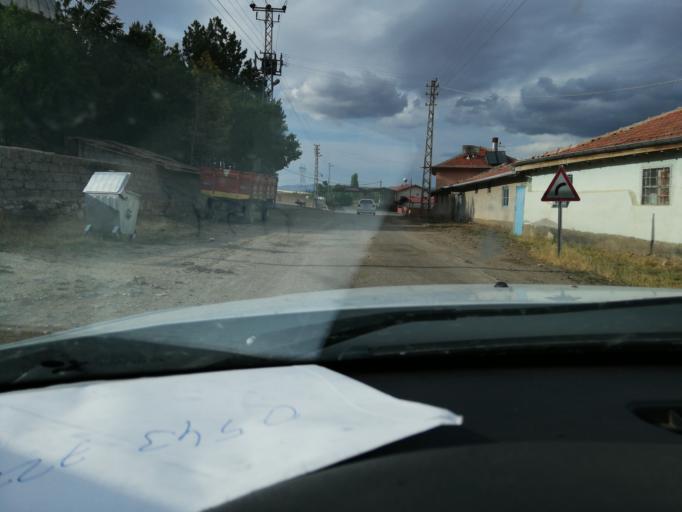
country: TR
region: Kirsehir
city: Kirsehir
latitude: 39.0280
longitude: 34.1268
